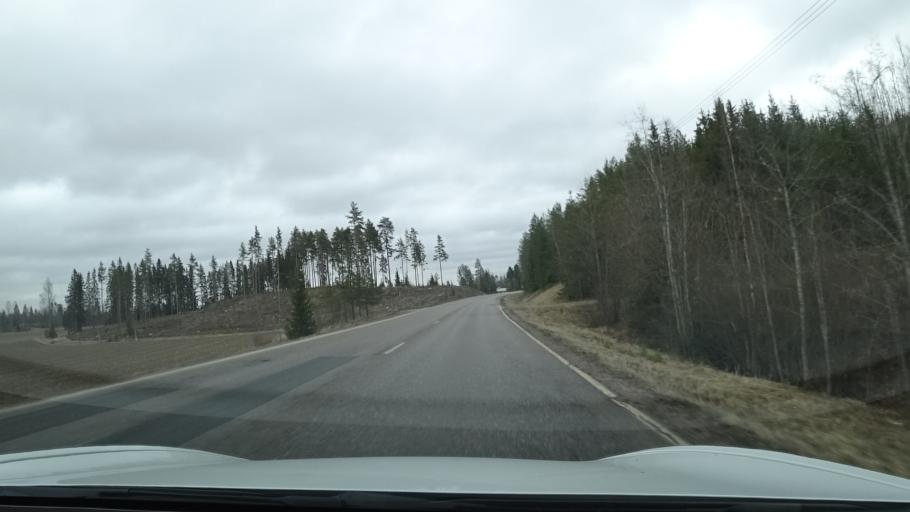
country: FI
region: Uusimaa
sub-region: Porvoo
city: Pukkila
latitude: 60.6513
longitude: 25.6627
